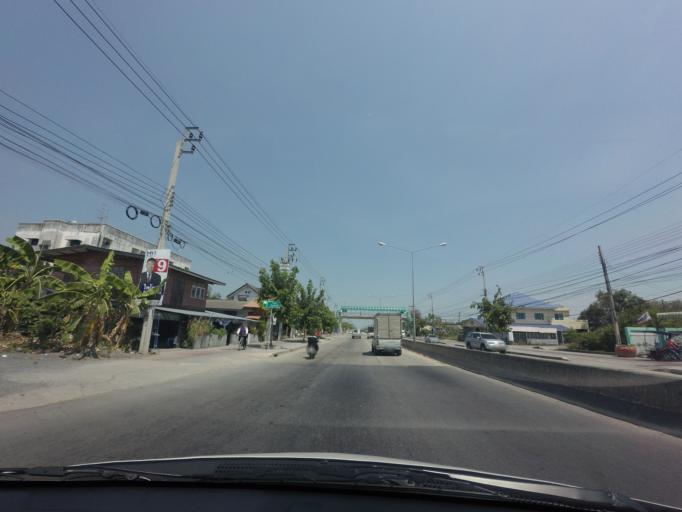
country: TH
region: Bangkok
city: Nong Chok
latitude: 13.8537
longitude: 100.8280
